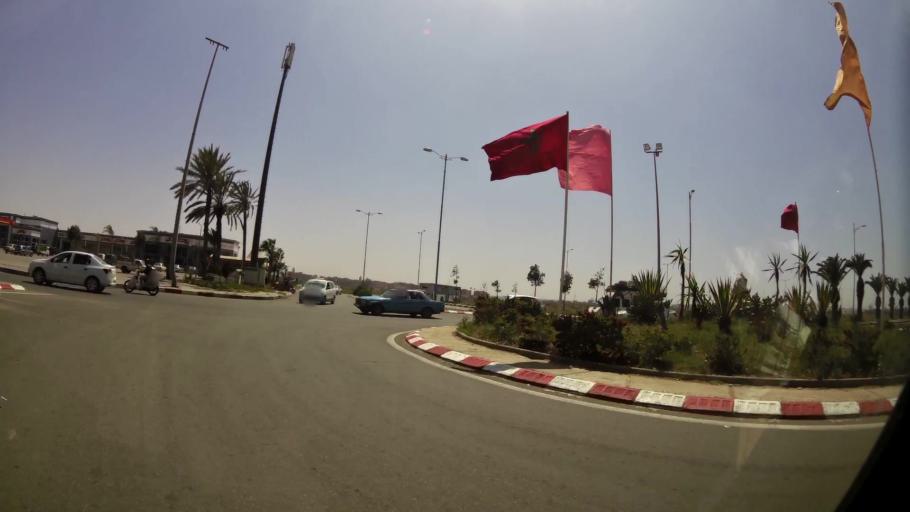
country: MA
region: Souss-Massa-Draa
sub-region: Inezgane-Ait Mellou
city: Inezgane
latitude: 30.3552
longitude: -9.5129
